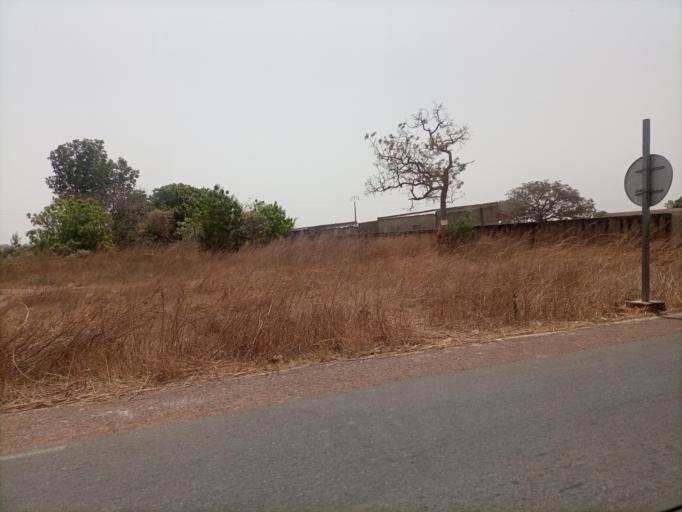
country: SN
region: Fatick
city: Sokone
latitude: 13.7296
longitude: -16.4220
